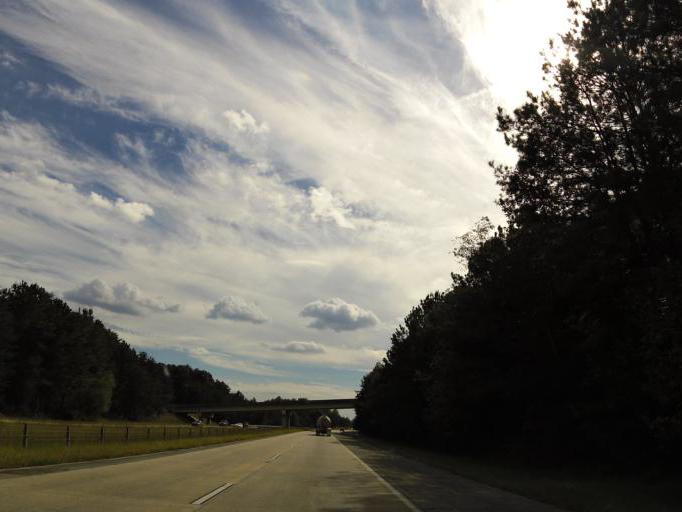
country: US
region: Georgia
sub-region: Cherokee County
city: Ball Ground
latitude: 34.3299
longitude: -84.3944
